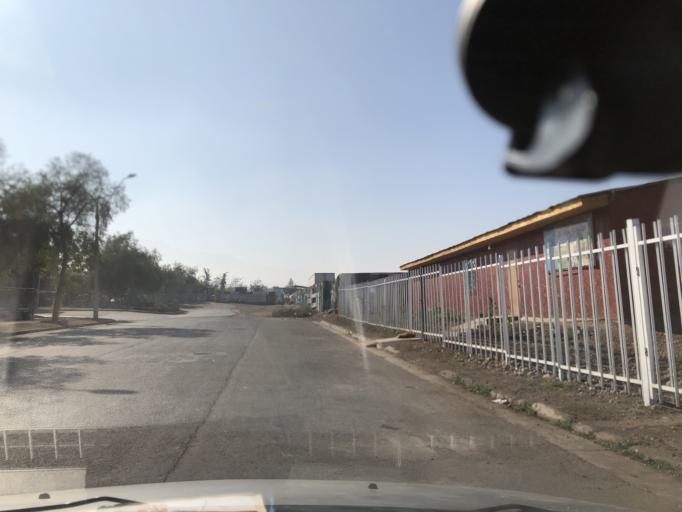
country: CL
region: Santiago Metropolitan
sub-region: Provincia de Cordillera
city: Puente Alto
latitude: -33.6307
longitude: -70.5875
